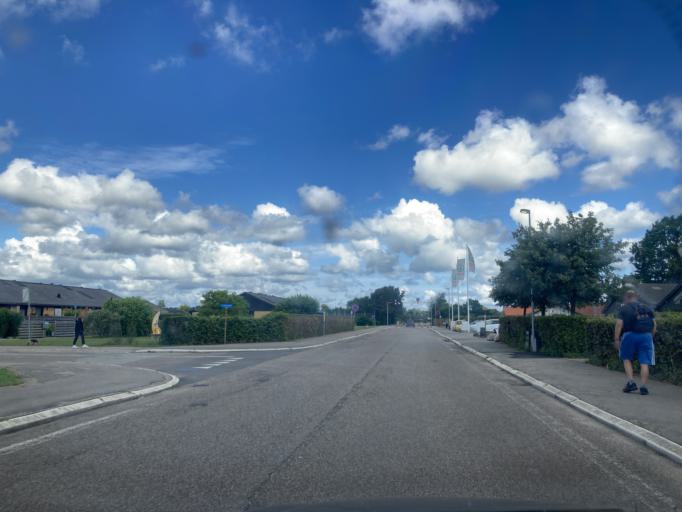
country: DK
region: Capital Region
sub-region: Halsnaes Kommune
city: Frederiksvaerk
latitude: 55.9842
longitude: 12.0119
